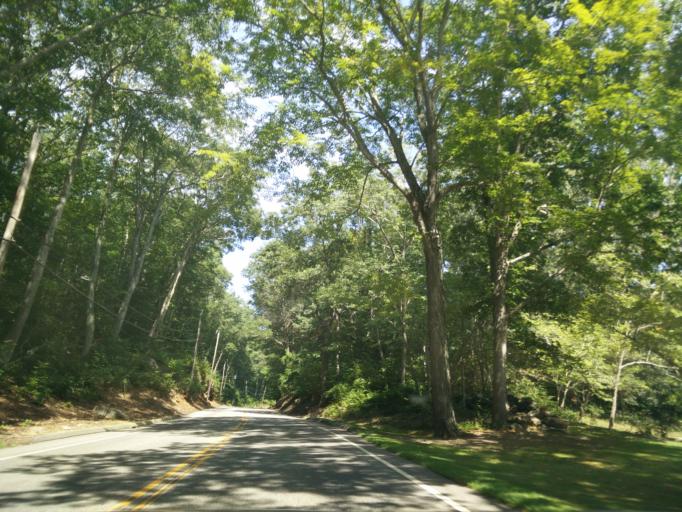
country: US
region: Connecticut
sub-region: Middlesex County
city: Clinton
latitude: 41.3290
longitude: -72.5503
